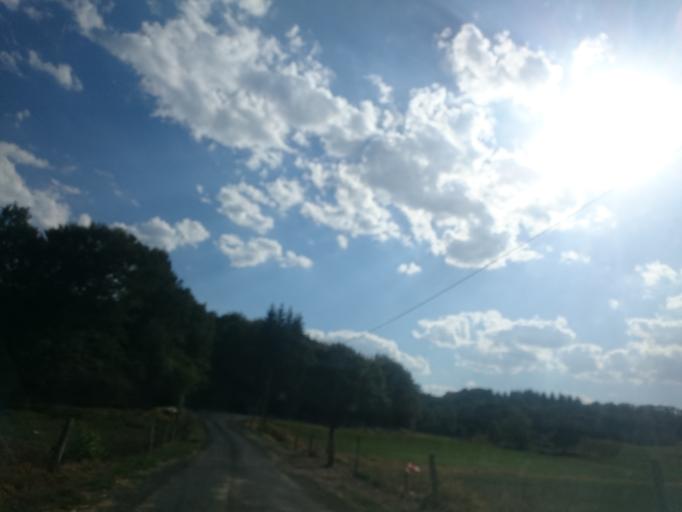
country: FR
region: Auvergne
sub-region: Departement du Cantal
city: Laroquebrou
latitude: 44.8953
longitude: 2.1712
